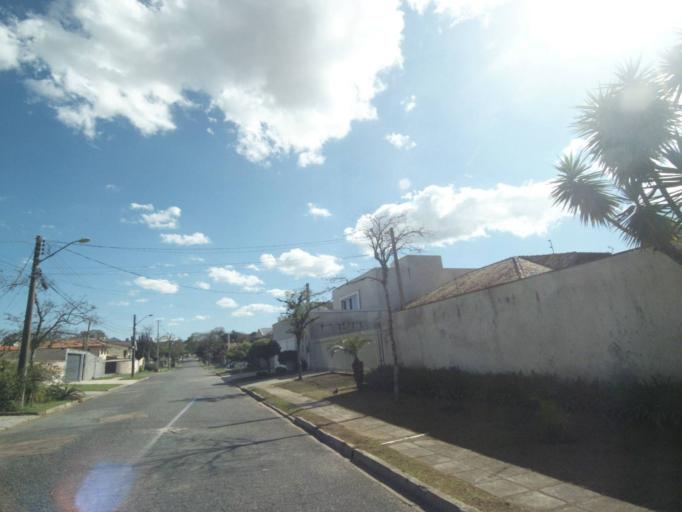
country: BR
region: Parana
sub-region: Curitiba
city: Curitiba
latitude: -25.3845
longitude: -49.2414
